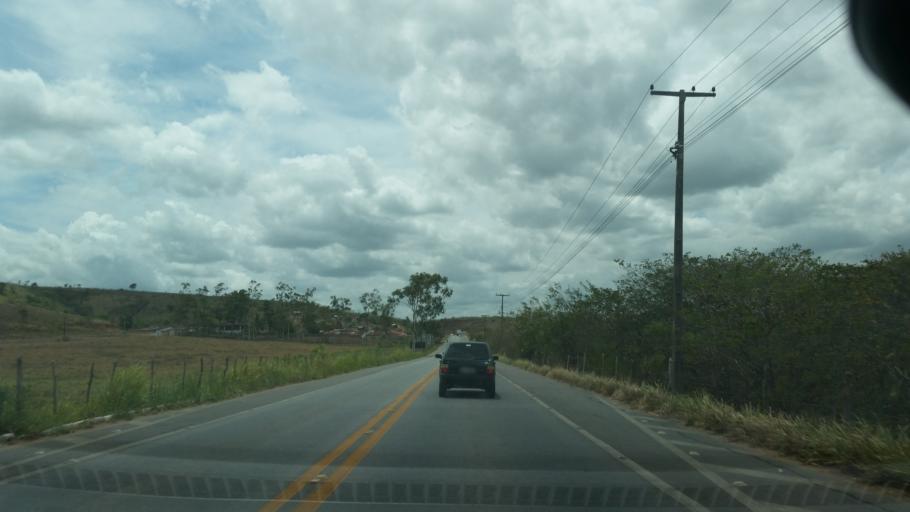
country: BR
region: Alagoas
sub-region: Uniao Dos Palmares
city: Uniao dos Palmares
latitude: -9.1765
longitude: -36.0312
